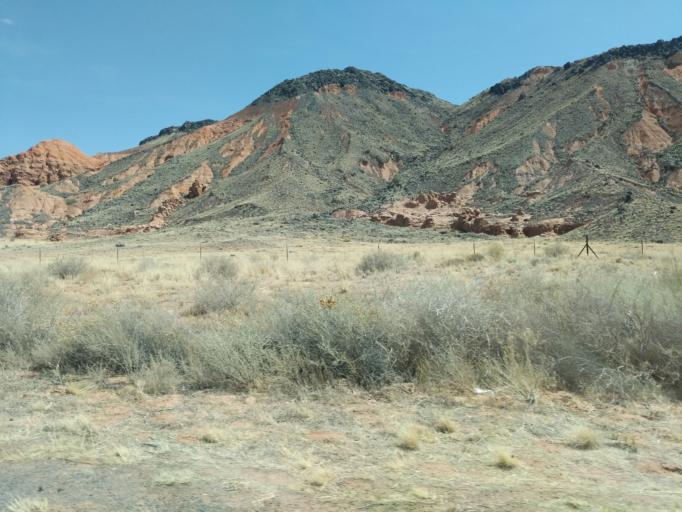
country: US
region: Arizona
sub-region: Navajo County
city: Dilkon
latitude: 35.4032
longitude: -110.0649
